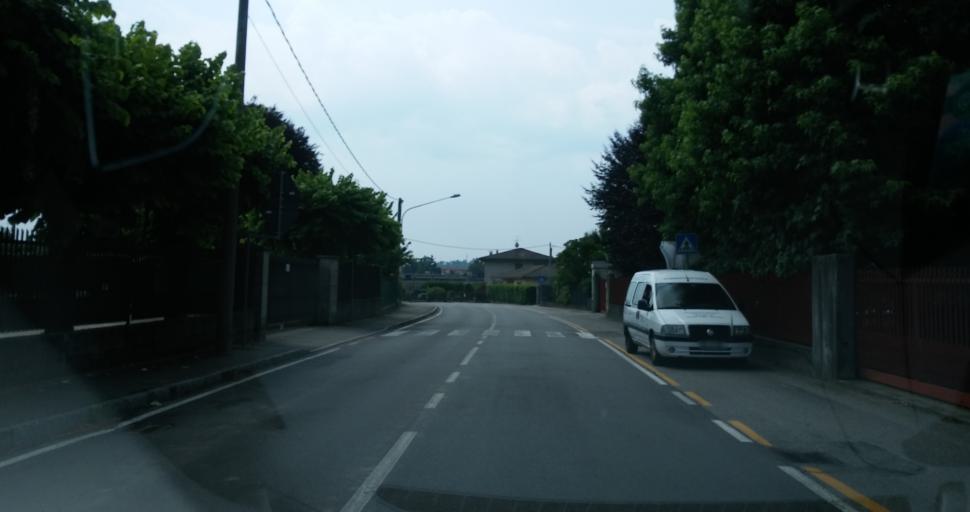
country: IT
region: Lombardy
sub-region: Provincia di Varese
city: Bardello
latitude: 45.8416
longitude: 8.6947
